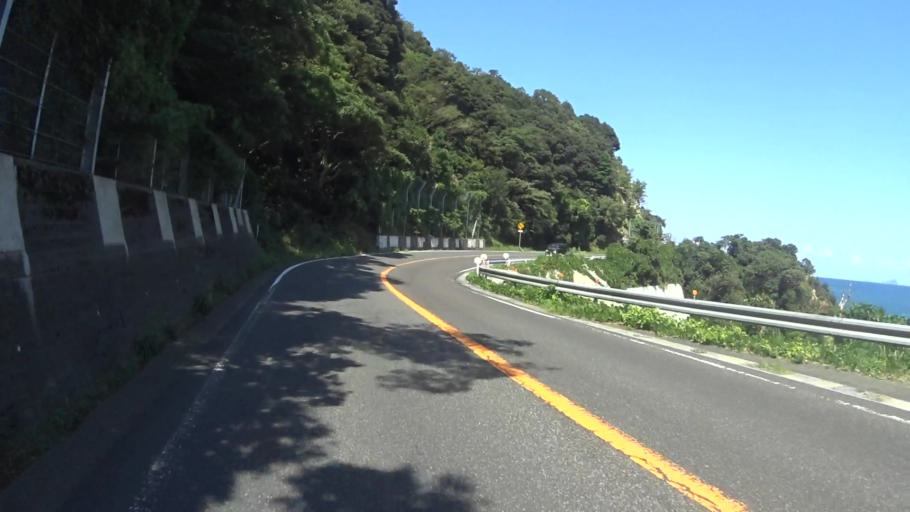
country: JP
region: Kyoto
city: Miyazu
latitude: 35.5313
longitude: 135.2694
